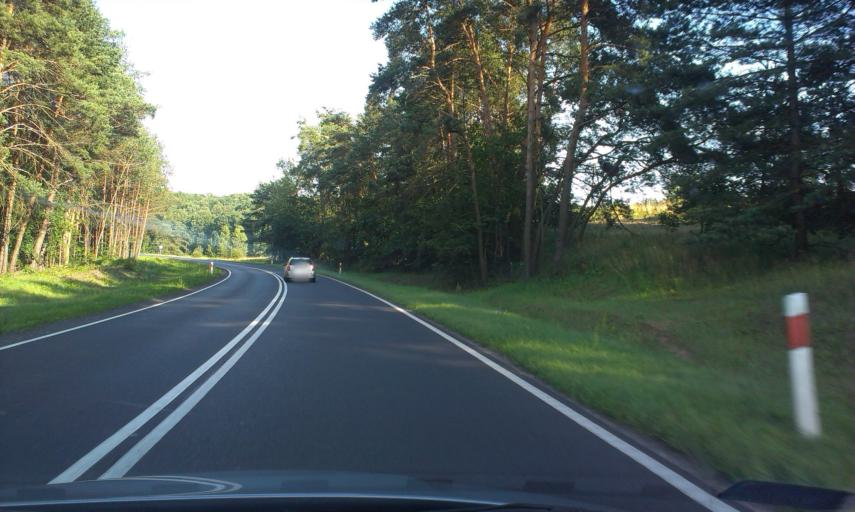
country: PL
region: Kujawsko-Pomorskie
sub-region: Powiat bydgoski
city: Sicienko
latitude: 53.1610
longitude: 17.7928
